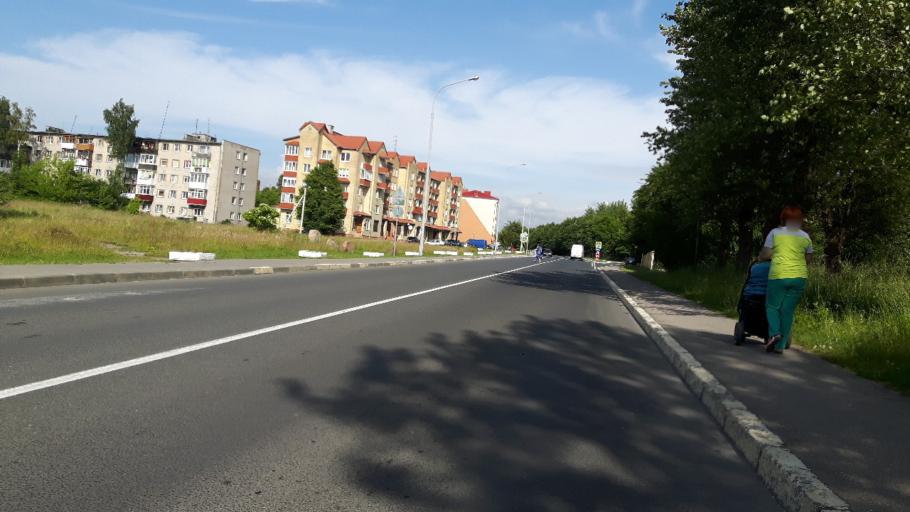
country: RU
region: Kaliningrad
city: Mamonovo
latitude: 54.4606
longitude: 19.9376
